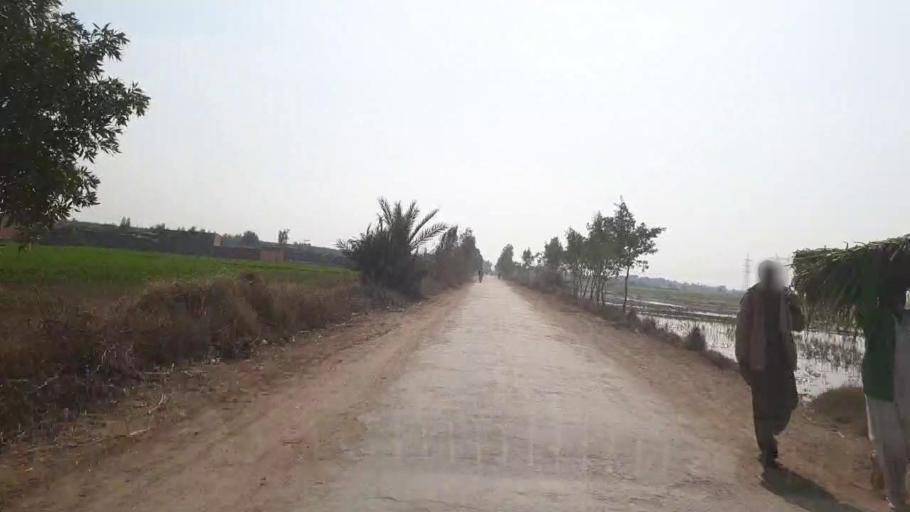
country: PK
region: Sindh
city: Bhit Shah
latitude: 25.7009
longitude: 68.5438
